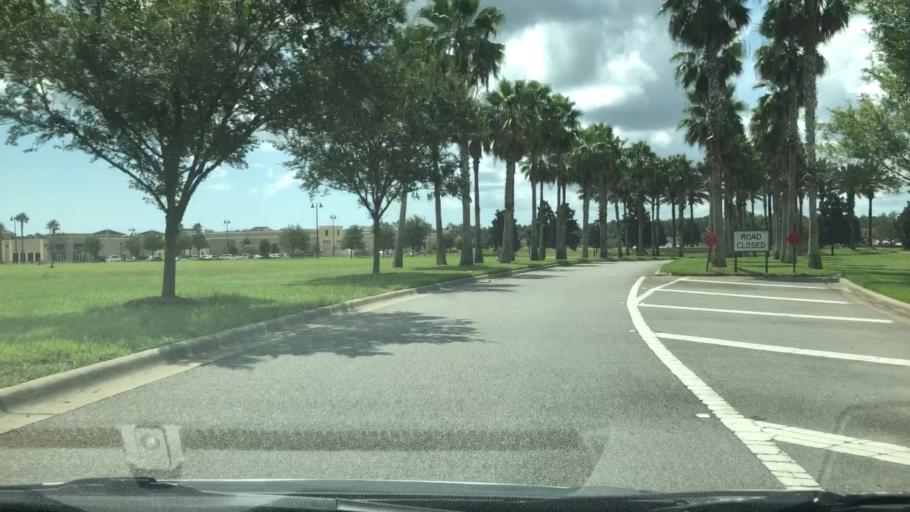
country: US
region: Florida
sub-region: Saint Johns County
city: Palm Valley
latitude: 30.1126
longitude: -81.4218
